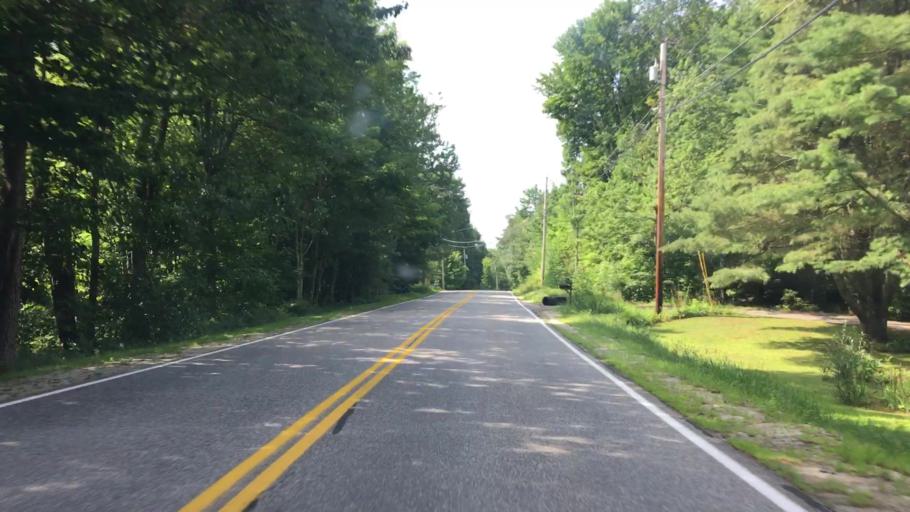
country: US
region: Maine
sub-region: Cumberland County
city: Raymond
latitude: 43.9388
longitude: -70.4382
